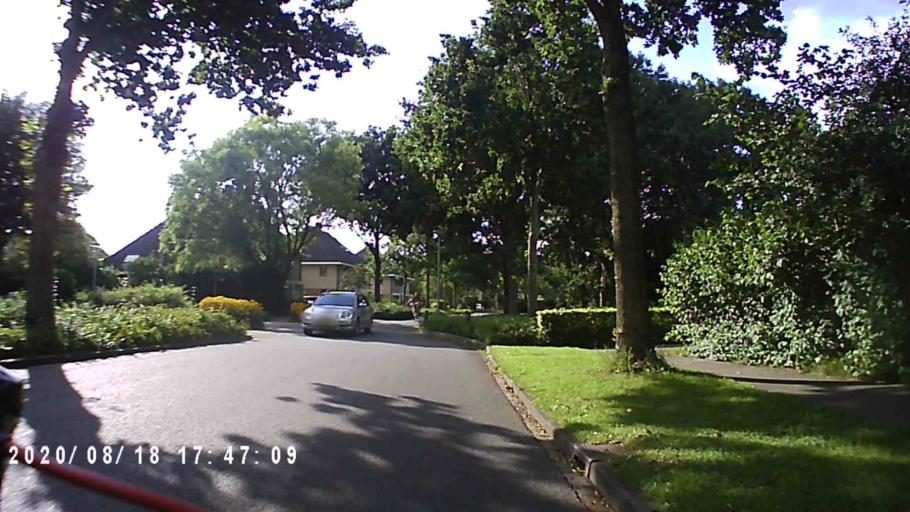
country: NL
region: Groningen
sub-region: Gemeente Zuidhorn
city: Zuidhorn
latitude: 53.2420
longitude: 6.3969
